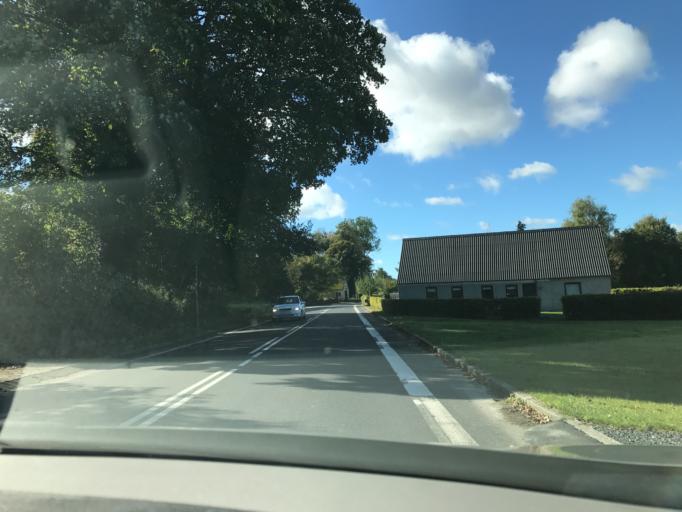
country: DK
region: South Denmark
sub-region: Assens Kommune
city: Tommerup
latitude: 55.2922
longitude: 10.2118
